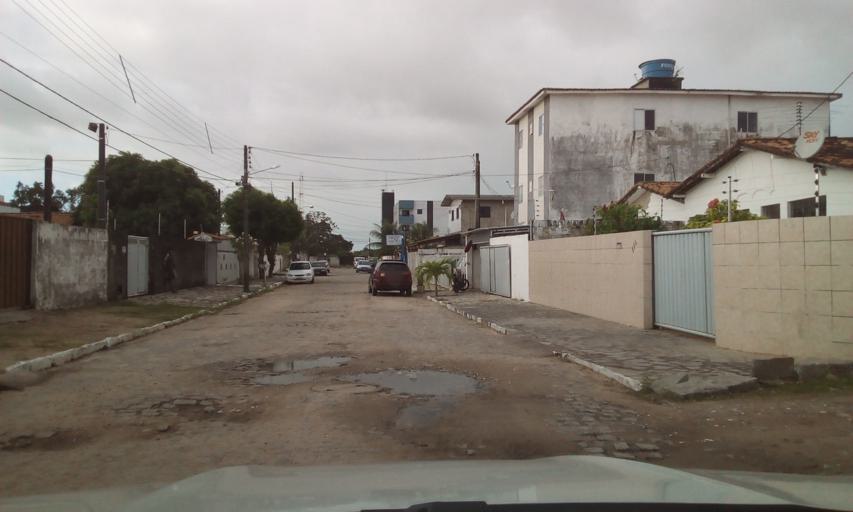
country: BR
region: Paraiba
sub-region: Joao Pessoa
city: Joao Pessoa
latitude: -7.1657
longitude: -34.8567
